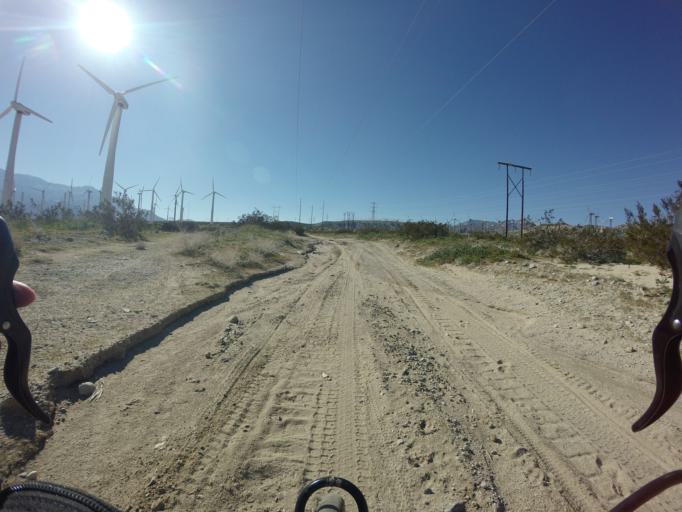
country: US
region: California
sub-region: Riverside County
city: Garnet
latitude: 33.9322
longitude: -116.6209
